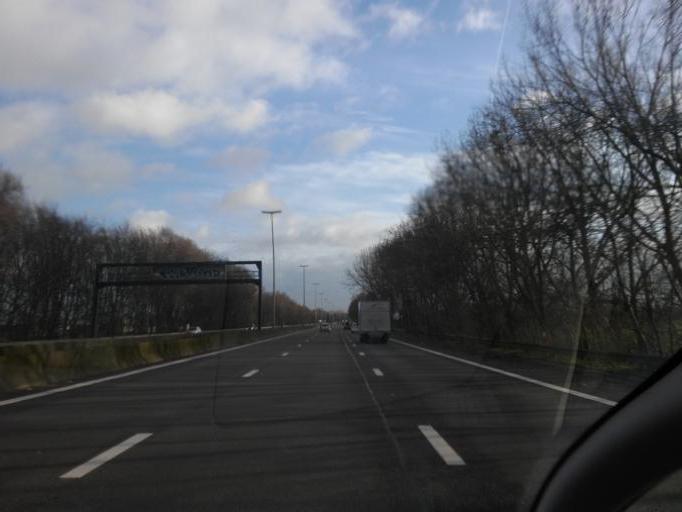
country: BE
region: Wallonia
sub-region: Province du Brabant Wallon
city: Walhain-Saint-Paul
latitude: 50.6504
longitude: 4.7037
